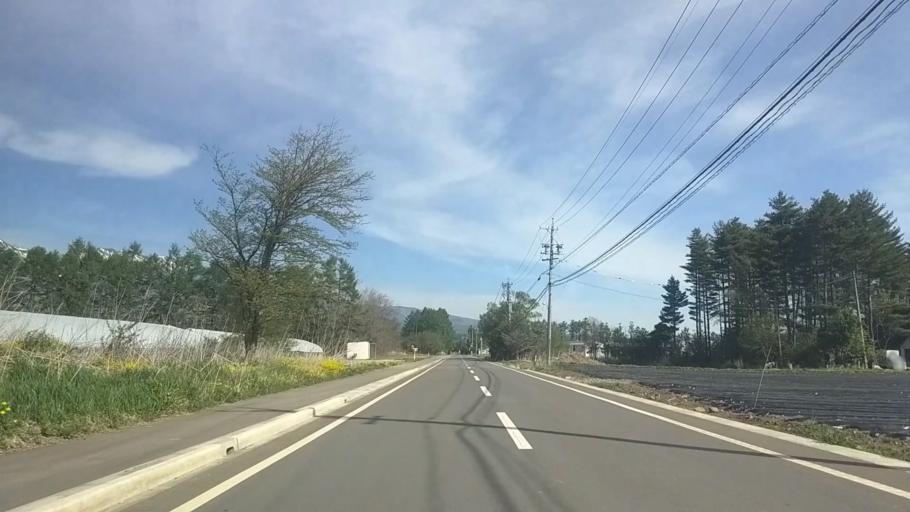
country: JP
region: Yamanashi
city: Nirasaki
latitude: 35.9482
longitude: 138.4763
